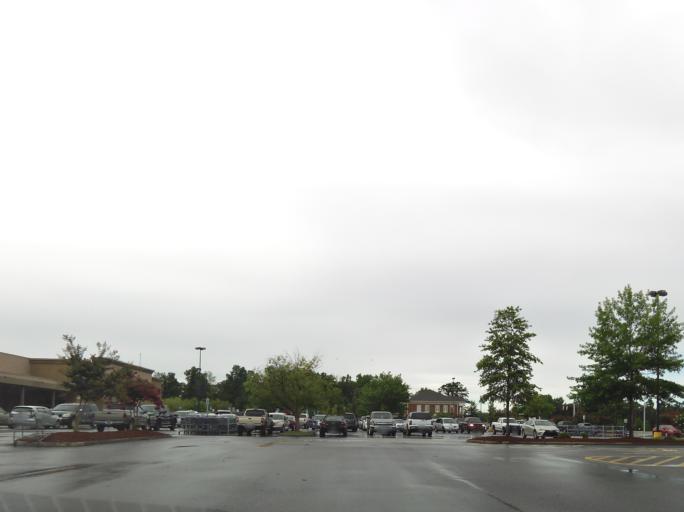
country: US
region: Georgia
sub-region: Lowndes County
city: Remerton
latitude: 30.8285
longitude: -83.3196
